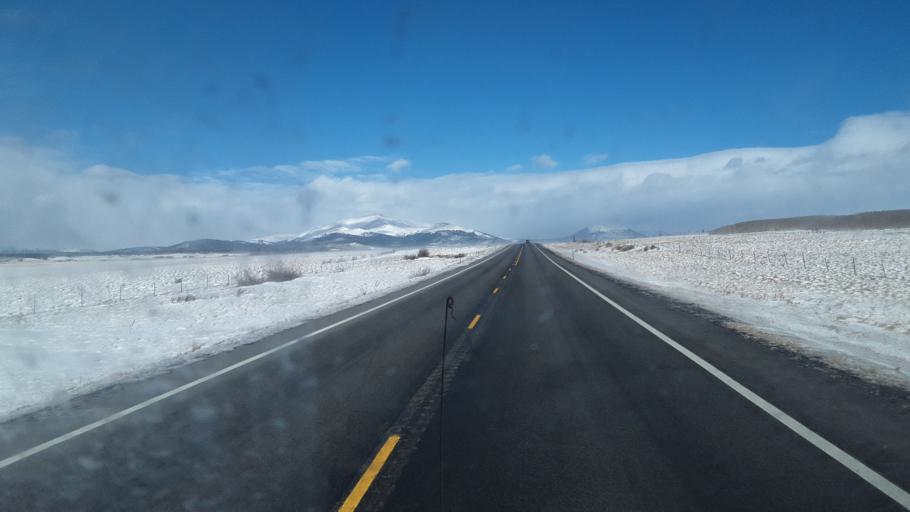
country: US
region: Colorado
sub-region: Park County
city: Fairplay
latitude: 39.1806
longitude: -105.9995
